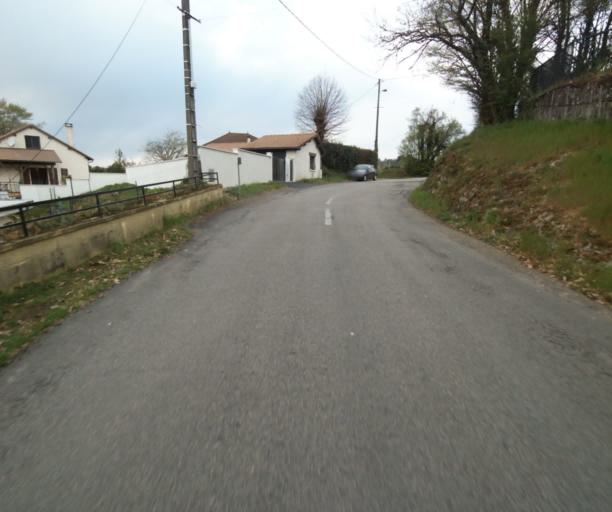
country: FR
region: Limousin
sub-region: Departement de la Correze
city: Tulle
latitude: 45.2580
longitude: 1.7648
